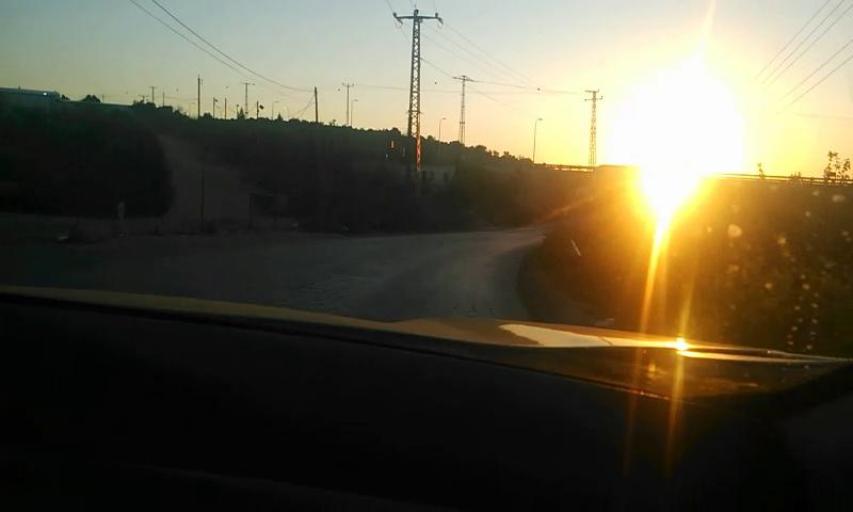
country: PS
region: West Bank
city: `Ayn Yabrud
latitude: 31.9589
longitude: 35.2580
